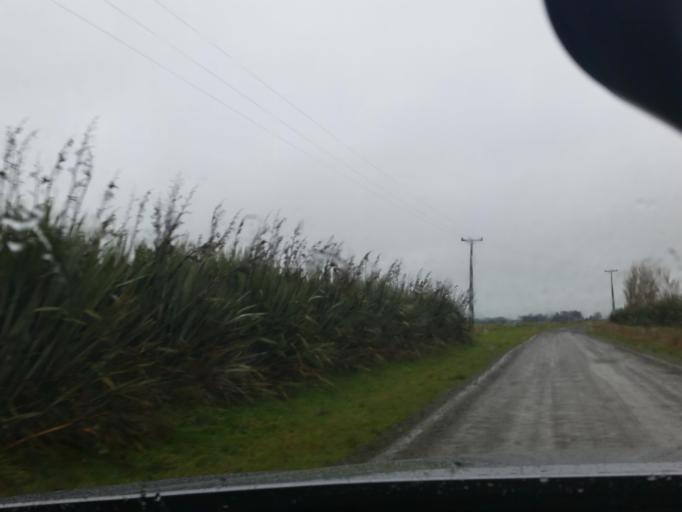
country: NZ
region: Southland
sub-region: Southland District
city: Winton
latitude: -46.1852
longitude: 168.2155
